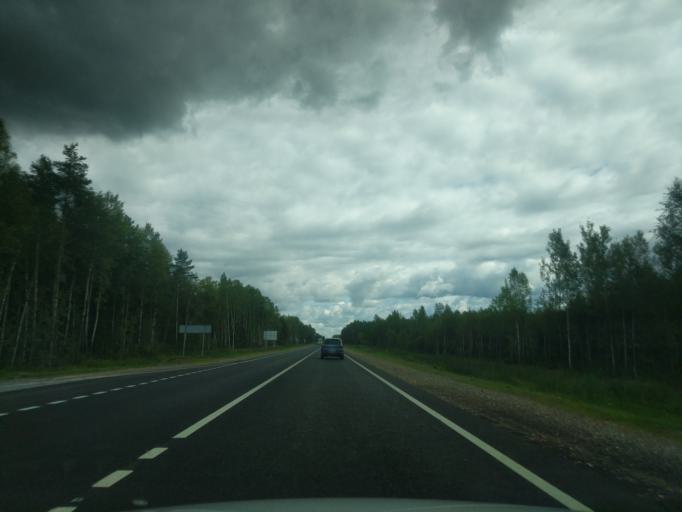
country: RU
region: Jaroslavl
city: Tunoshna
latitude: 57.5494
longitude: 40.1744
